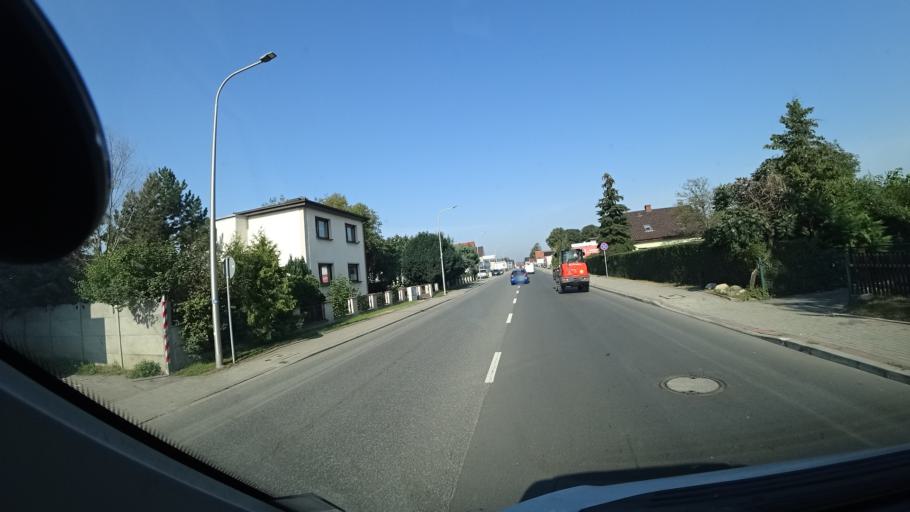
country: PL
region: Opole Voivodeship
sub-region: Powiat kedzierzynsko-kozielski
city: Kozle
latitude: 50.3422
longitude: 18.1732
